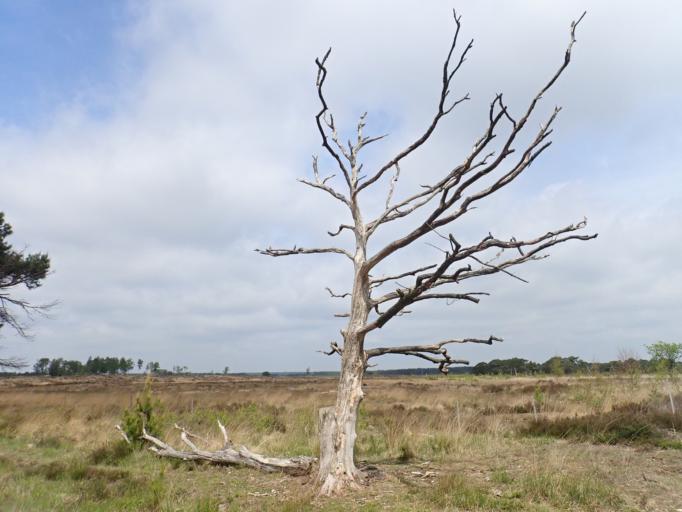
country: BE
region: Flanders
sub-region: Provincie Antwerpen
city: Kalmthout
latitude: 51.3859
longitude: 4.4364
